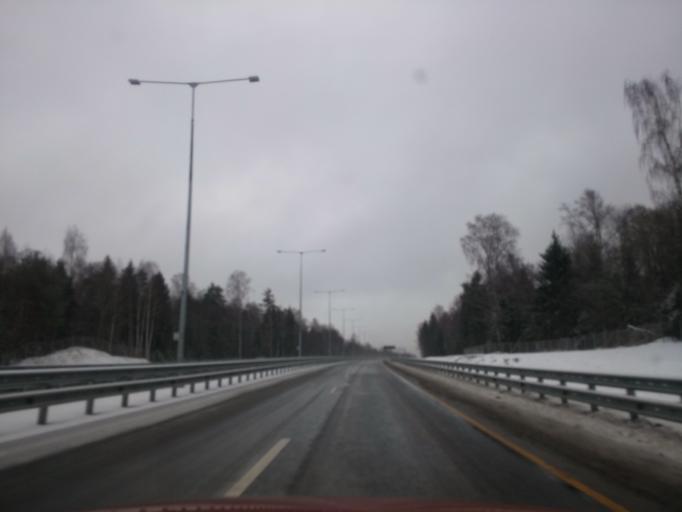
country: RU
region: Tverskaya
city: Likhoslavl'
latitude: 56.9694
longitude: 35.4620
